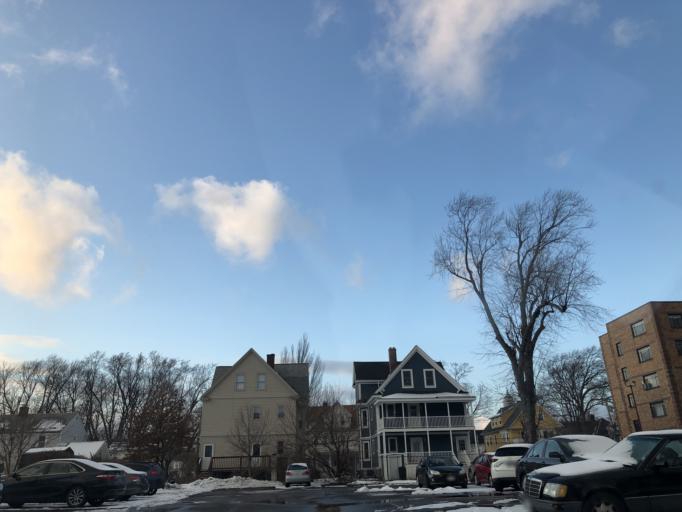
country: US
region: Massachusetts
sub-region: Middlesex County
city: Arlington
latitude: 42.4075
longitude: -71.1460
